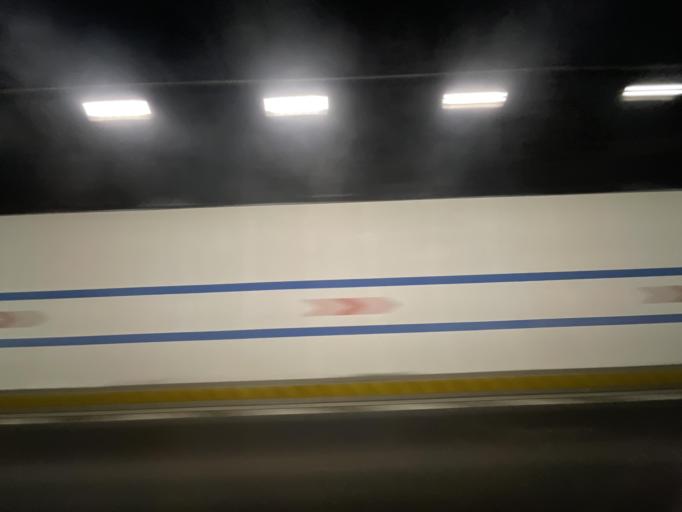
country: CN
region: Guangdong
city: Humen
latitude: 22.8066
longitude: 113.6544
